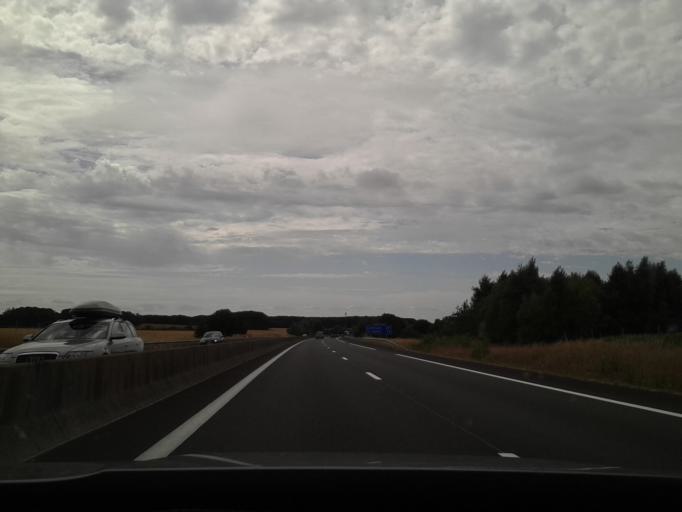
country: FR
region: Pays de la Loire
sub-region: Departement de la Sarthe
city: Beaumont-sur-Sarthe
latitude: 48.3044
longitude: 0.1477
